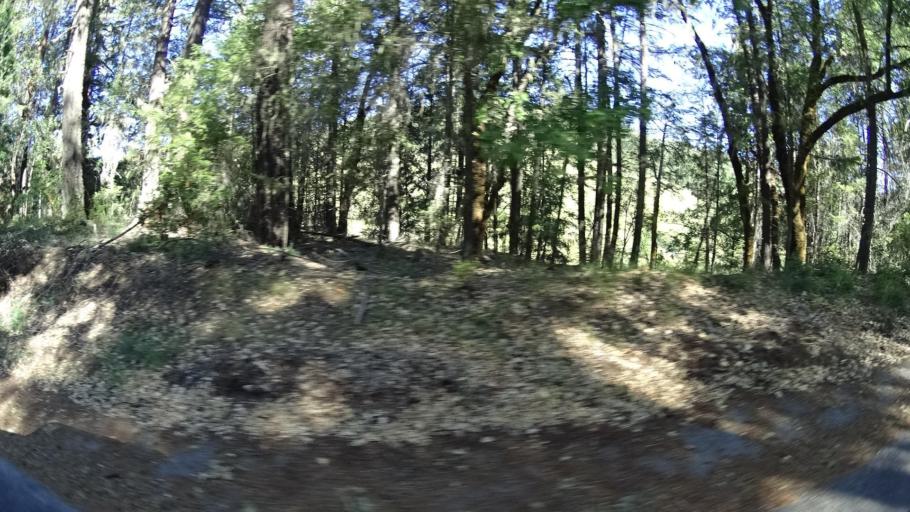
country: US
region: California
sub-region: Lake County
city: Upper Lake
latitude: 39.4087
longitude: -122.9806
